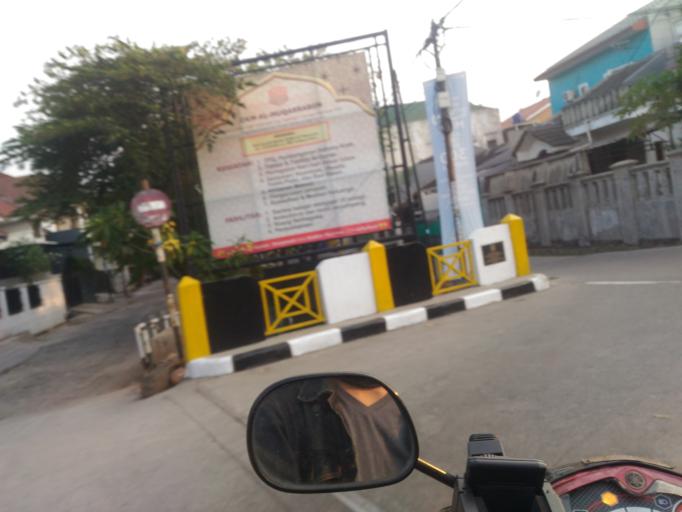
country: ID
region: West Java
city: Depok
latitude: -6.3648
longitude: 106.8549
